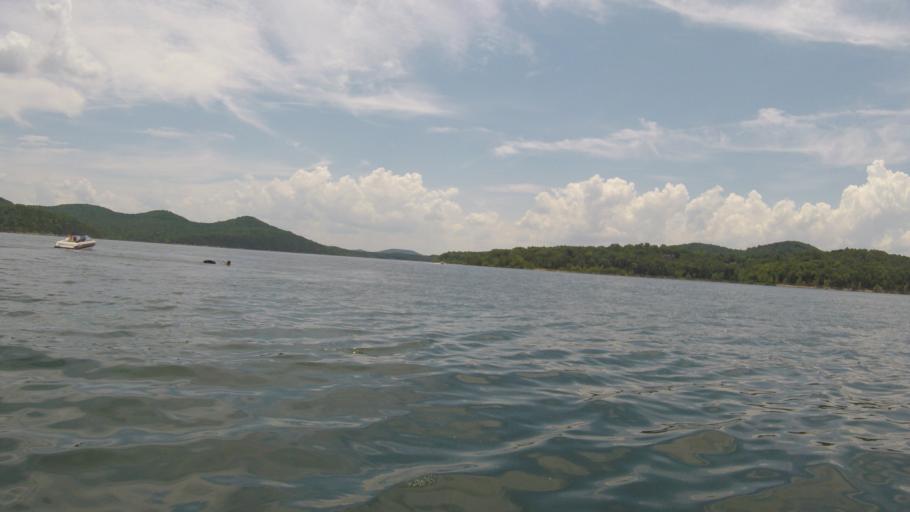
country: US
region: Missouri
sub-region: Barry County
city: Shell Knob
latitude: 36.6178
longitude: -93.5442
